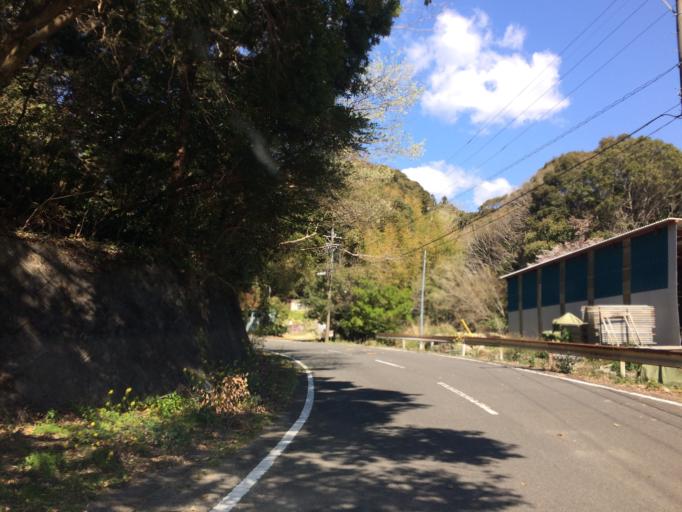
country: JP
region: Shizuoka
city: Fujieda
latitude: 34.8536
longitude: 138.2234
